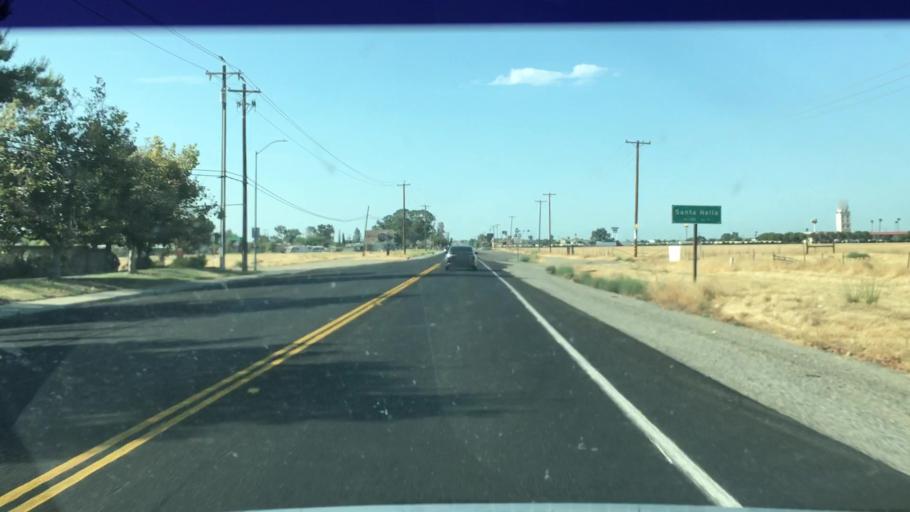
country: US
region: California
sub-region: Merced County
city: Gustine
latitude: 37.0928
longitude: -121.0160
